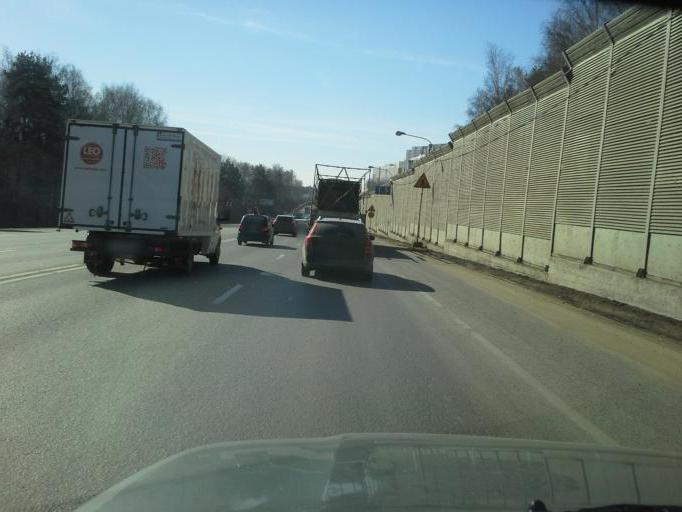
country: RU
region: Moskovskaya
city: Odintsovo
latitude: 55.6677
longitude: 37.3091
